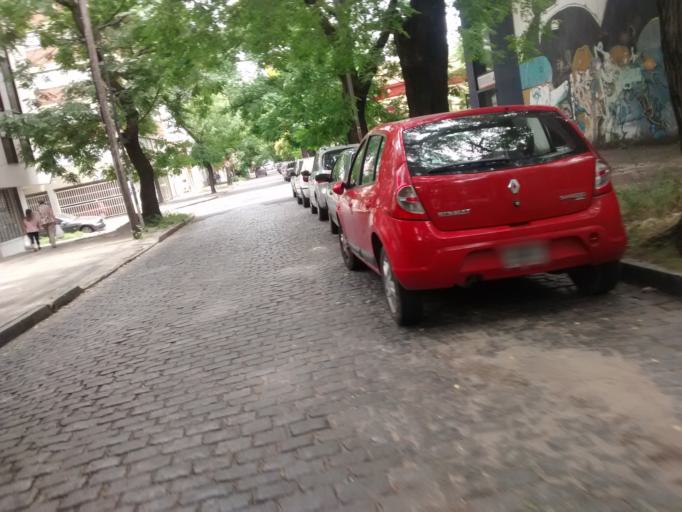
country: AR
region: Buenos Aires
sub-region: Partido de La Plata
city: La Plata
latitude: -34.9208
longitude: -57.9600
